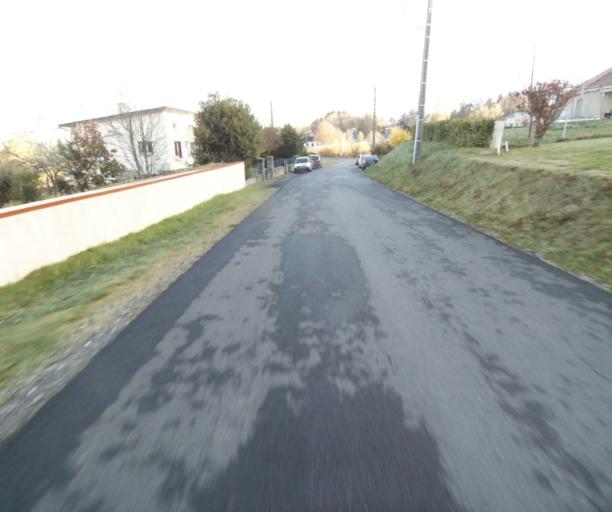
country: FR
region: Limousin
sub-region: Departement de la Correze
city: Correze
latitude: 45.3161
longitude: 1.8425
